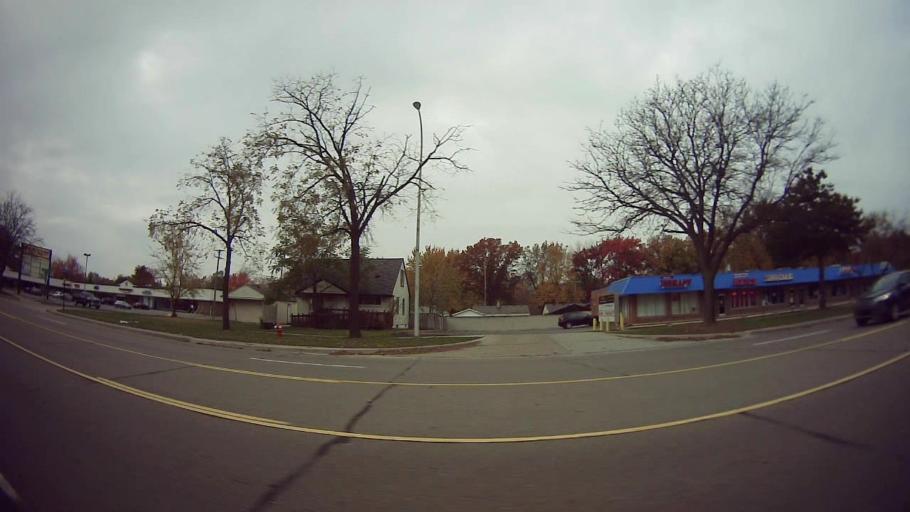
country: US
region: Michigan
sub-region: Oakland County
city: Madison Heights
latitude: 42.4959
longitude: -83.1053
